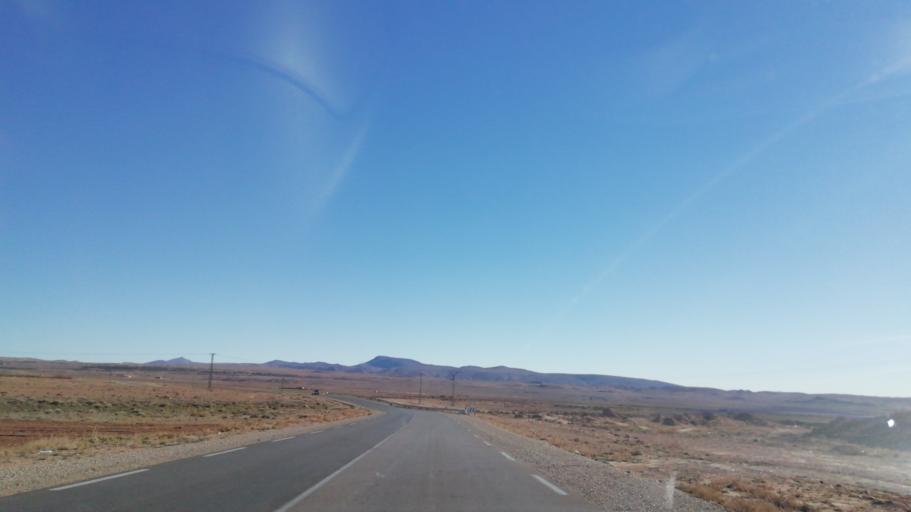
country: DZ
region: El Bayadh
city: El Bayadh
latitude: 33.6037
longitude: 1.2871
